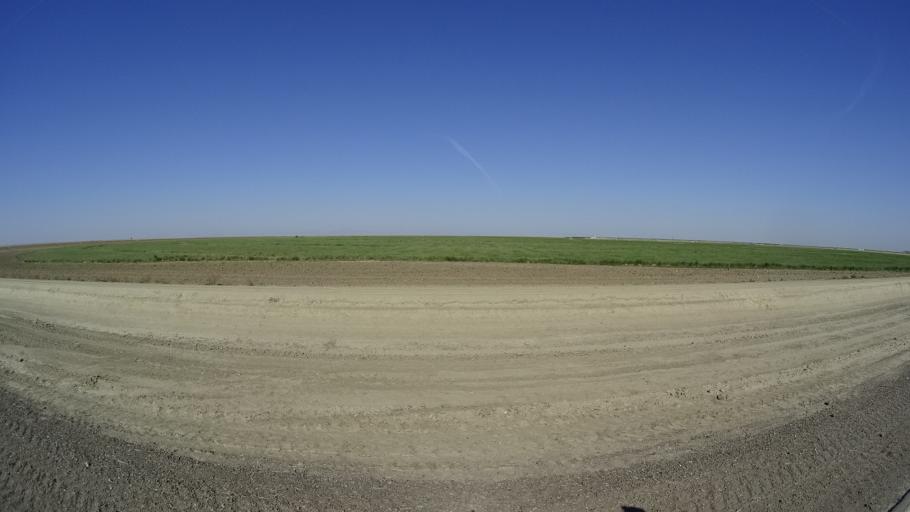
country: US
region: California
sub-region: Kings County
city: Corcoran
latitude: 36.0530
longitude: -119.5719
